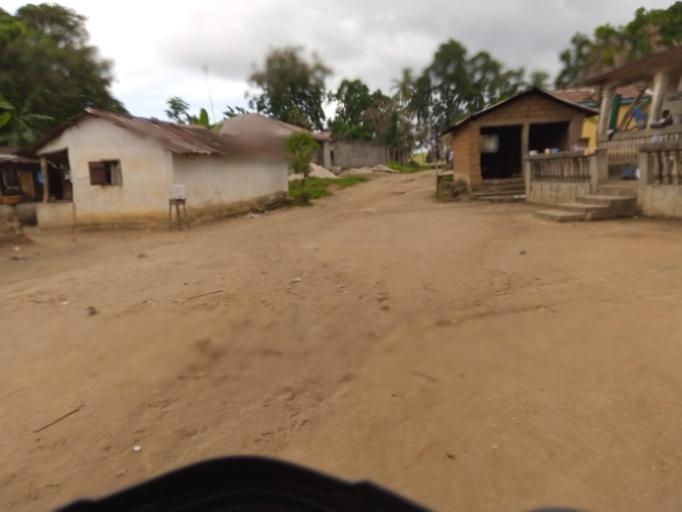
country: SL
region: Northern Province
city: Masoyila
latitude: 8.5754
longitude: -13.1623
